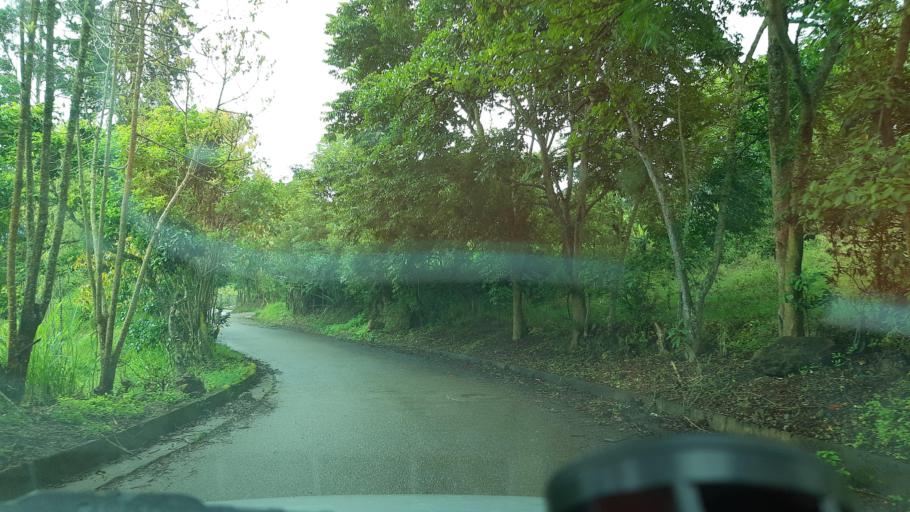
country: CO
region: Cundinamarca
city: Manta
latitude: 5.0515
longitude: -73.5070
